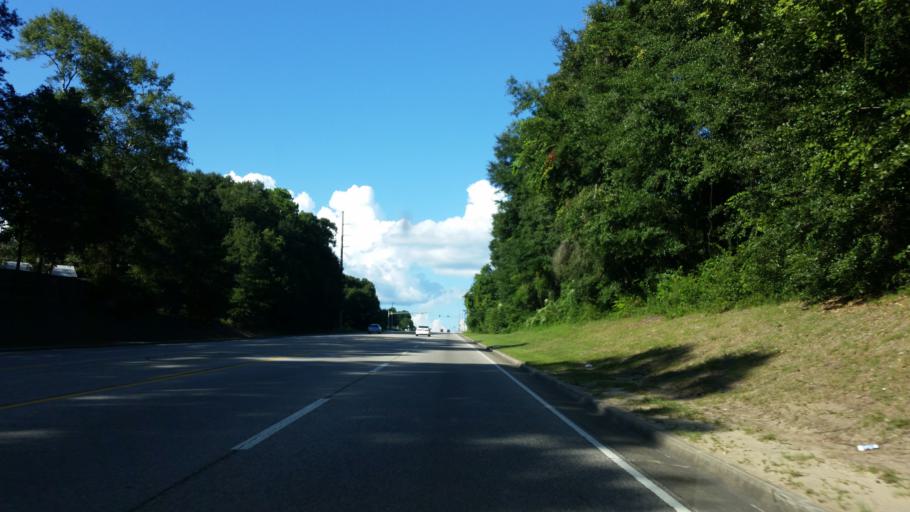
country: US
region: Alabama
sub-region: Mobile County
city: Prichard
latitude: 30.7149
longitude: -88.1664
